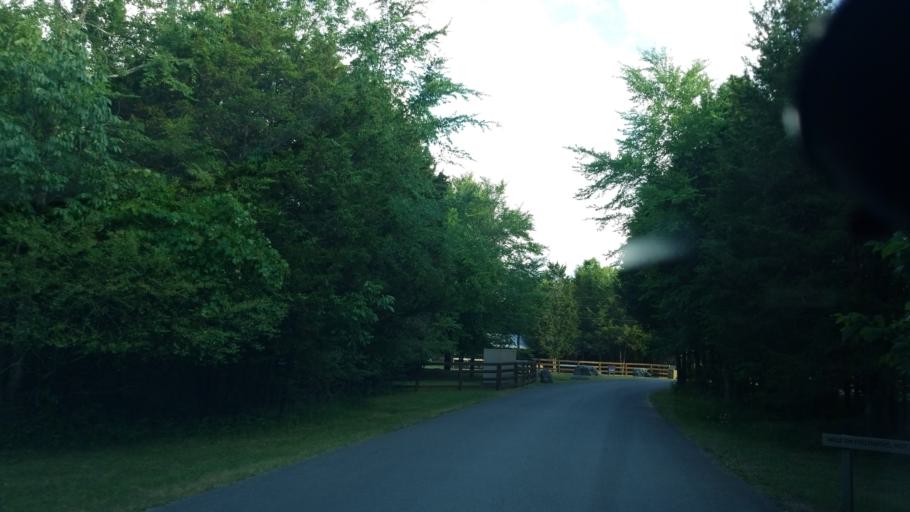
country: US
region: Tennessee
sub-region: Rutherford County
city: La Vergne
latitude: 36.0892
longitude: -86.5854
